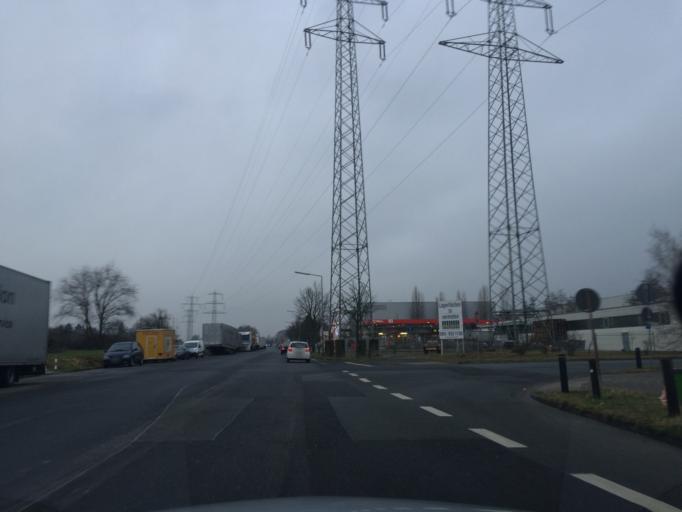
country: DE
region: Hesse
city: Morfelden-Walldorf
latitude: 49.9824
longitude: 8.5794
